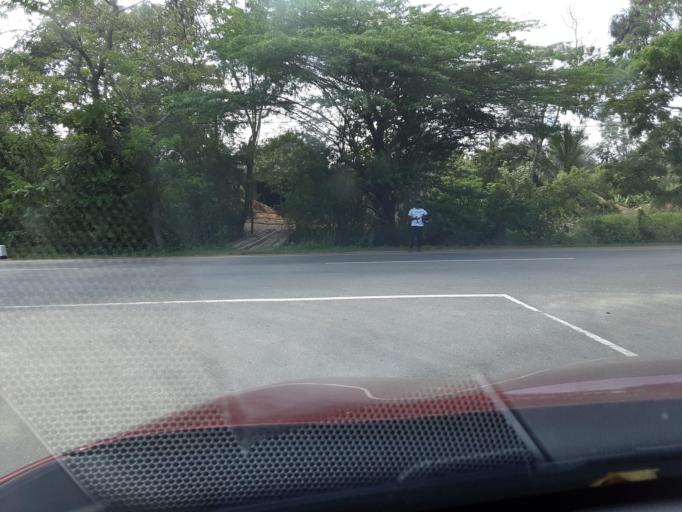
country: LK
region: Southern
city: Tangalla
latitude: 6.2115
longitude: 81.2043
